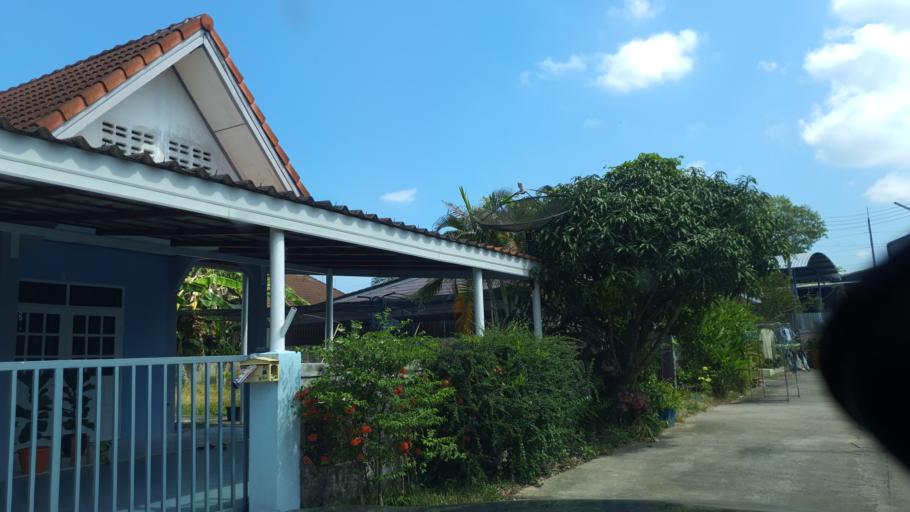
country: TH
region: Krabi
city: Nuea Khlong
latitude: 8.0830
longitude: 98.9890
